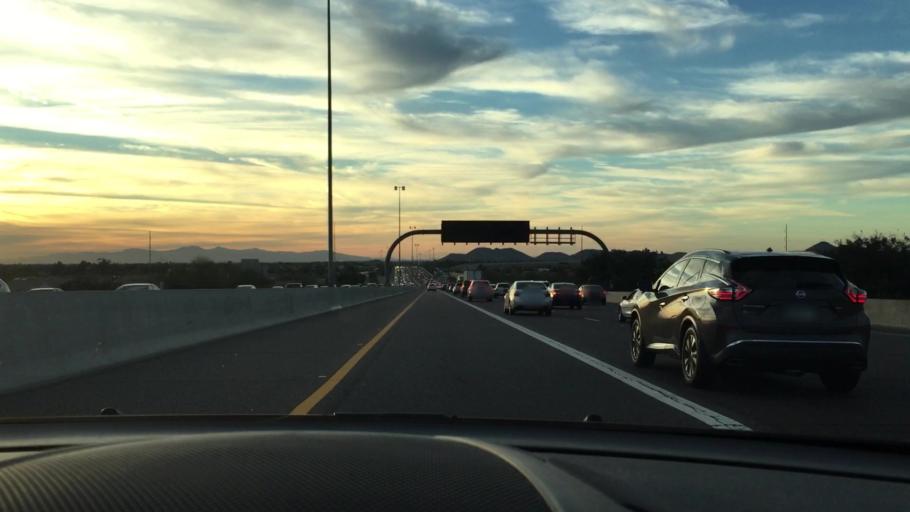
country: US
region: Arizona
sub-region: Maricopa County
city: Paradise Valley
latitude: 33.6670
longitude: -112.0513
